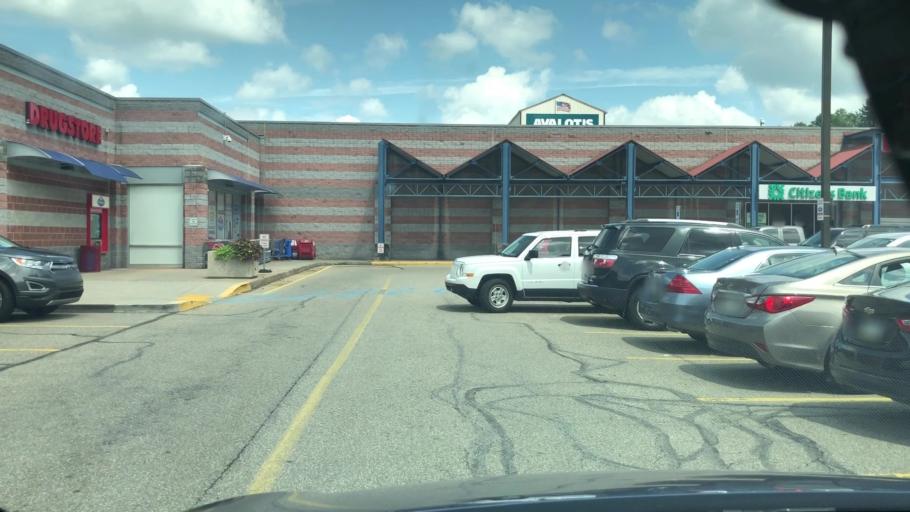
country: US
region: Pennsylvania
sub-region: Allegheny County
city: Penn Hills
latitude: 40.4986
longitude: -79.8447
